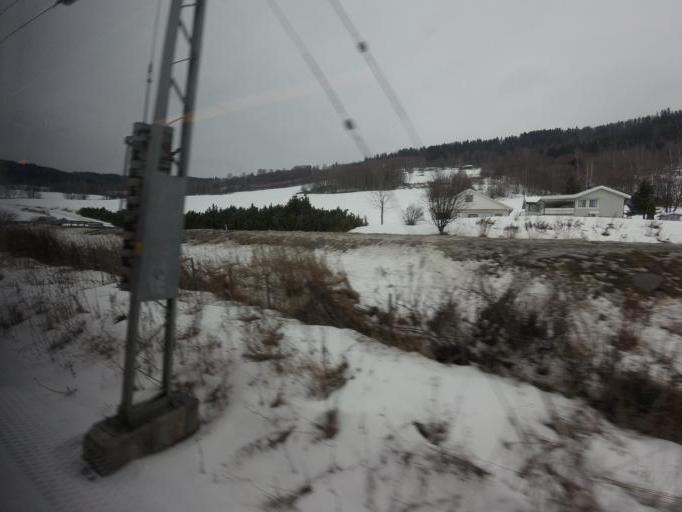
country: NO
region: Hedmark
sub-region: Ringsaker
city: Moelv
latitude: 60.9792
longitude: 10.6505
